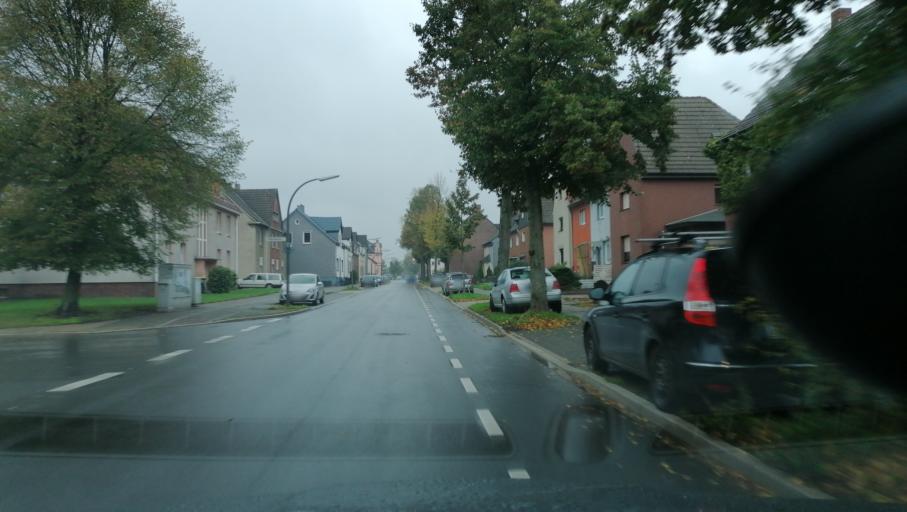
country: DE
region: North Rhine-Westphalia
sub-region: Regierungsbezirk Arnsberg
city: Herne
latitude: 51.5665
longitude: 7.2026
